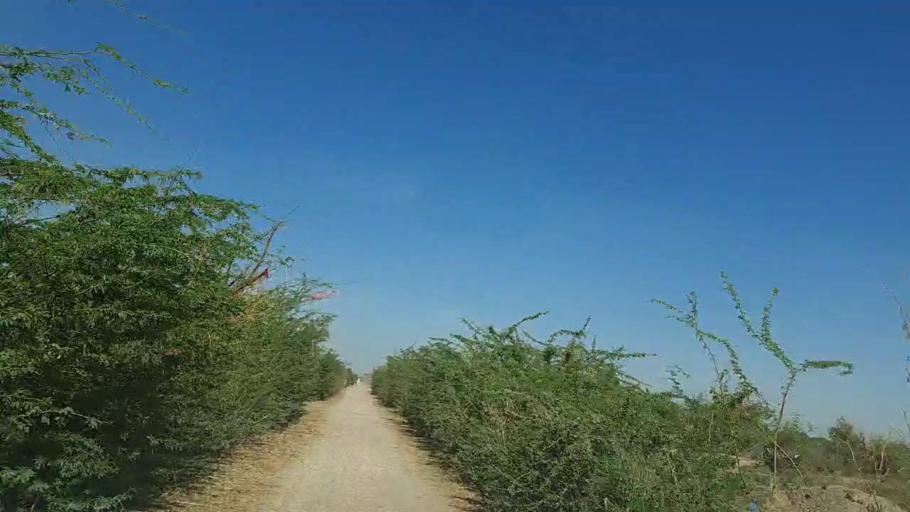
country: PK
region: Sindh
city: Dhoro Naro
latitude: 25.5119
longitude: 69.5285
